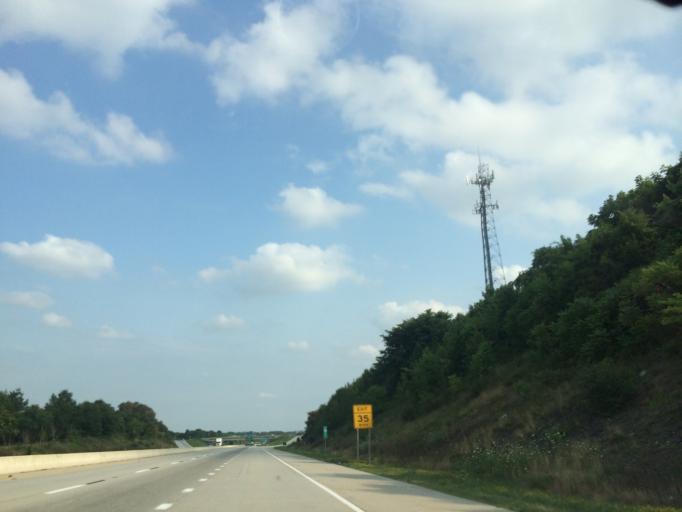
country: US
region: Pennsylvania
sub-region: Cumberland County
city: Mechanicsburg
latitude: 40.2626
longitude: -76.9966
